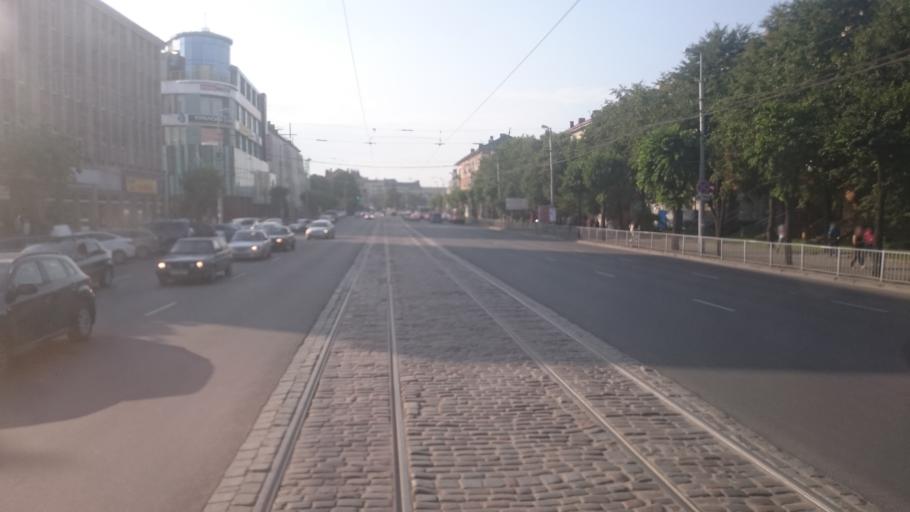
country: RU
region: Kaliningrad
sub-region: Gorod Kaliningrad
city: Kaliningrad
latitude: 54.7136
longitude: 20.5063
